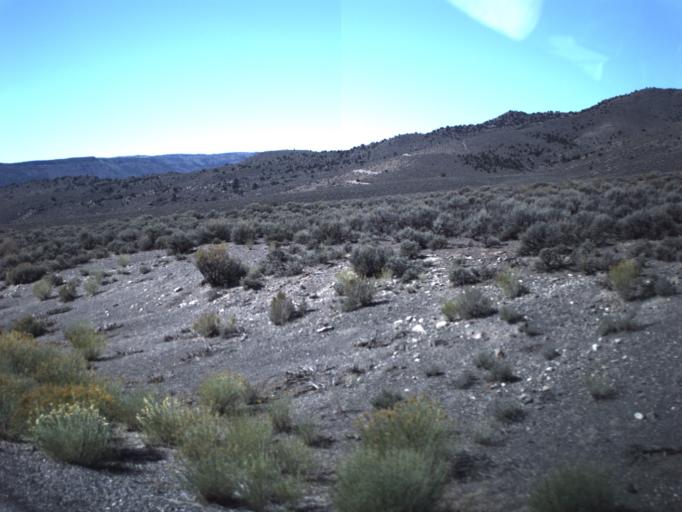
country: US
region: Utah
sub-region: Piute County
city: Junction
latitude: 38.1830
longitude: -112.0164
